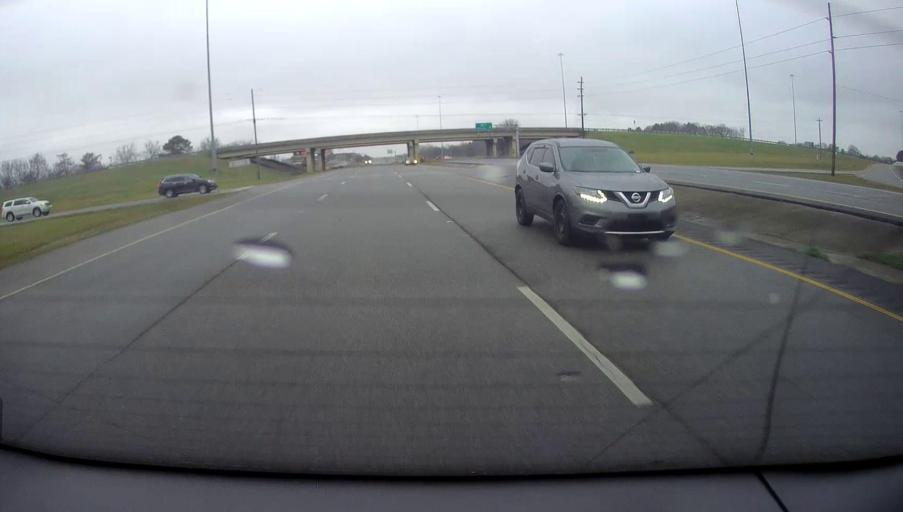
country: US
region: Alabama
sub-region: Morgan County
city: Decatur
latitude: 34.6003
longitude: -87.0314
